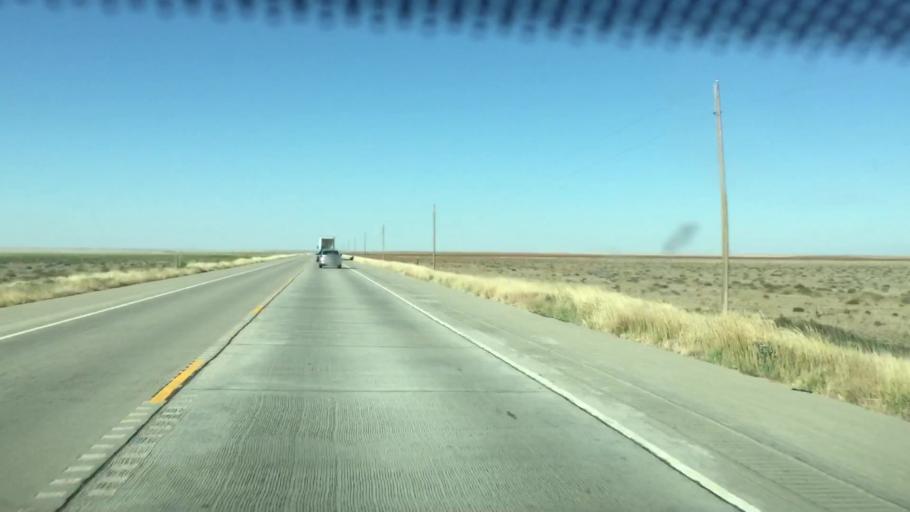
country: US
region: Colorado
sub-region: Kiowa County
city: Eads
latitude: 38.2839
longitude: -102.7199
